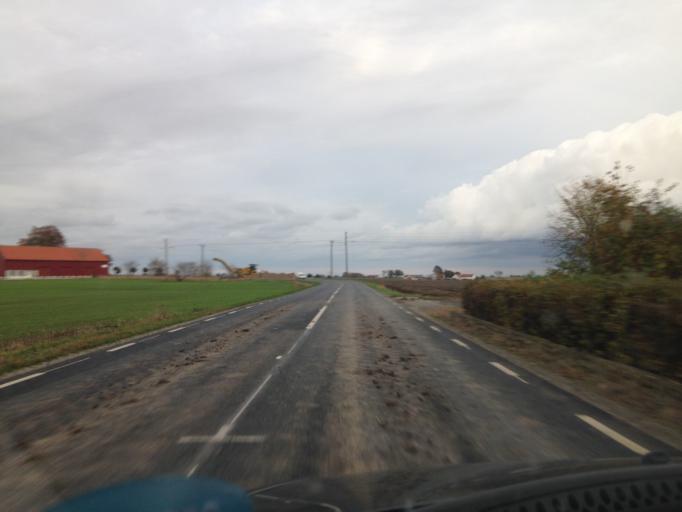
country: SE
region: Skane
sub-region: Simrishamns Kommun
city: Simrishamn
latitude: 55.4299
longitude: 14.1686
